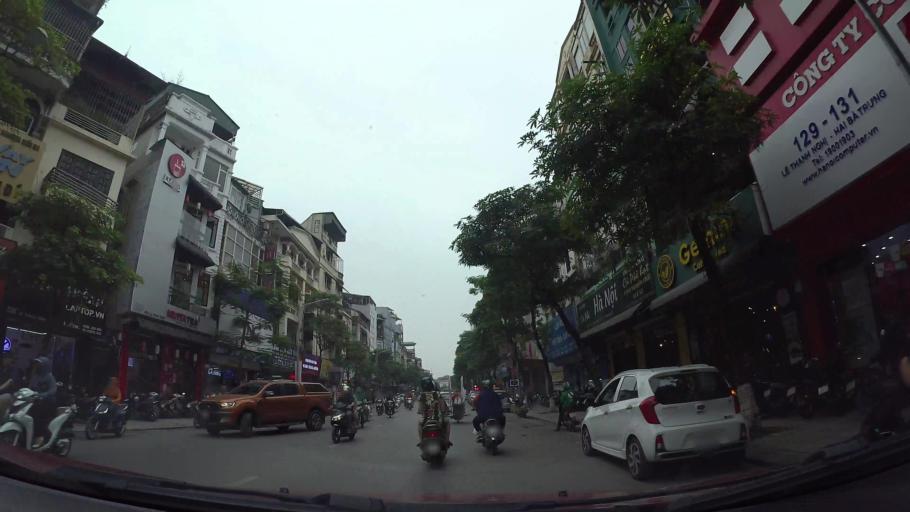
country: VN
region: Ha Noi
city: Hai BaTrung
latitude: 21.0018
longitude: 105.8428
